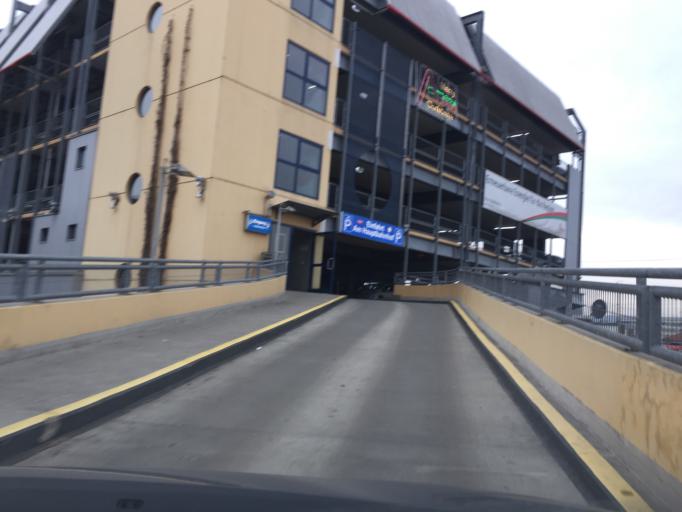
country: DE
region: Bavaria
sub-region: Regierungsbezirk Unterfranken
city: Aschaffenburg
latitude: 49.9797
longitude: 9.1490
